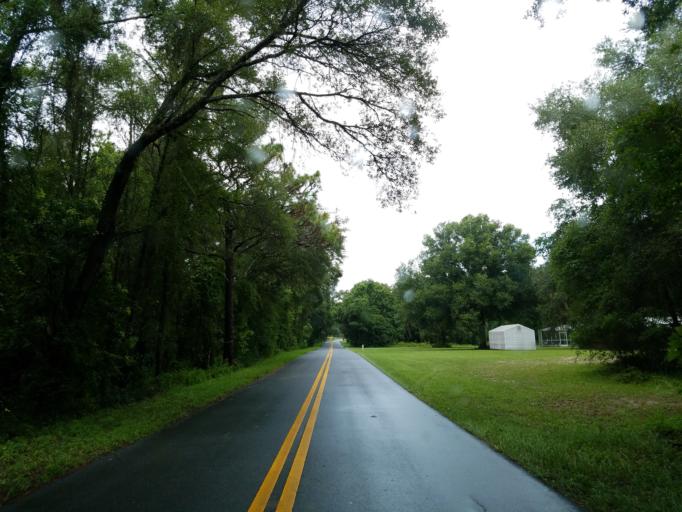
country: US
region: Florida
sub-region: Citrus County
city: Floral City
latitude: 28.7863
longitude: -82.2940
